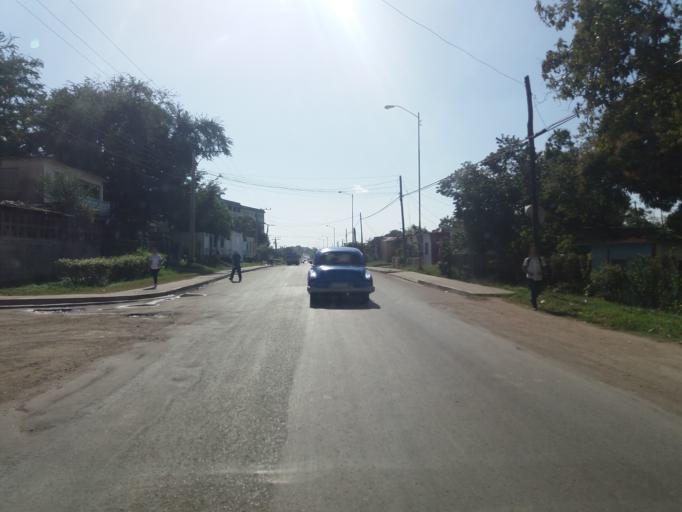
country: CU
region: Cienfuegos
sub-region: Municipio de Cienfuegos
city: Cienfuegos
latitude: 22.1555
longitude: -80.4326
